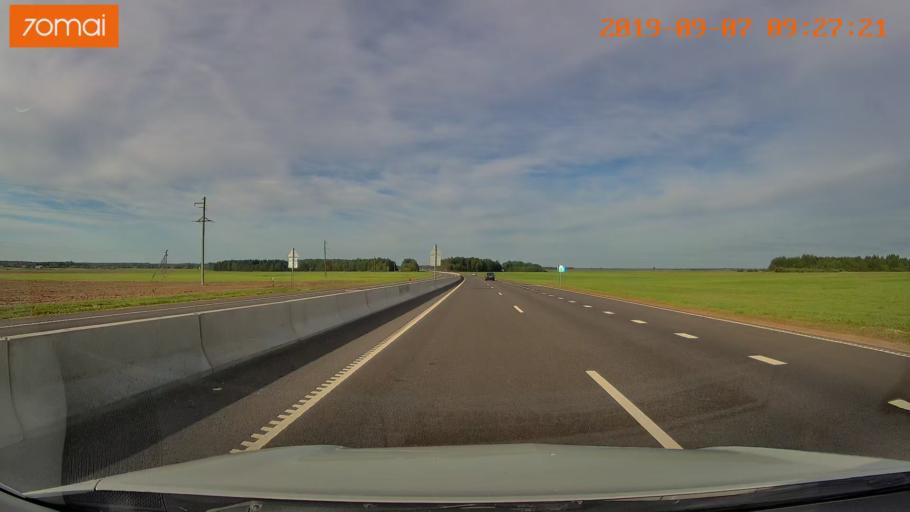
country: BY
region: Grodnenskaya
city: Lyubcha
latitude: 53.9125
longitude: 26.0796
